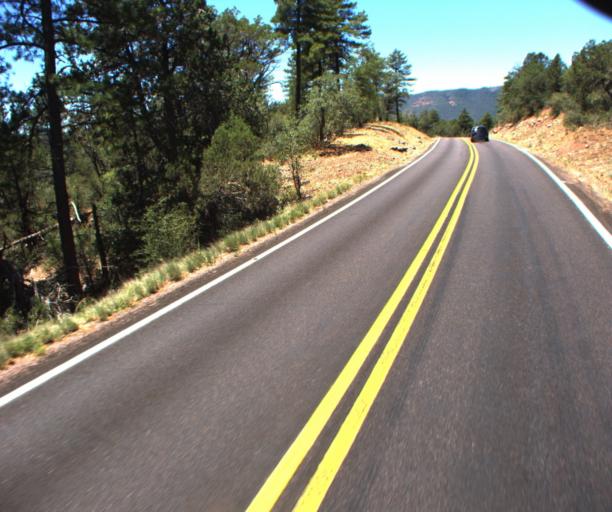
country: US
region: Arizona
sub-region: Gila County
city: Pine
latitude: 34.3634
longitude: -111.4284
